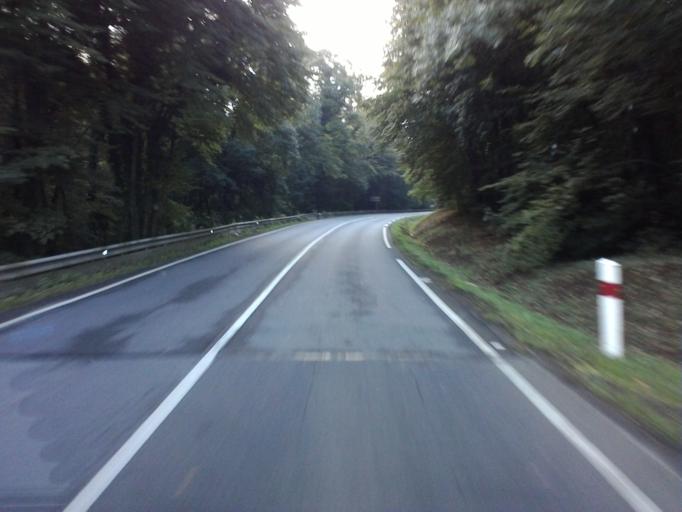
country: FR
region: Lorraine
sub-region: Departement de Meurthe-et-Moselle
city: Longuyon
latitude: 49.4662
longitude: 5.5948
